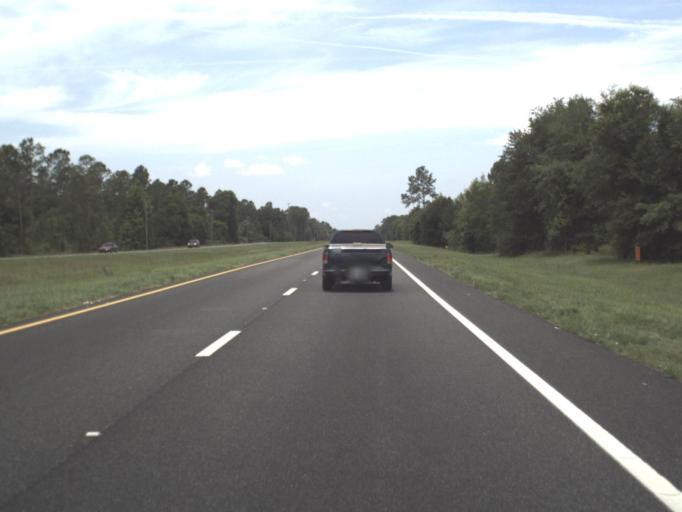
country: US
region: Florida
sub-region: Alachua County
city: Hawthorne
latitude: 29.6010
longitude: -82.1972
